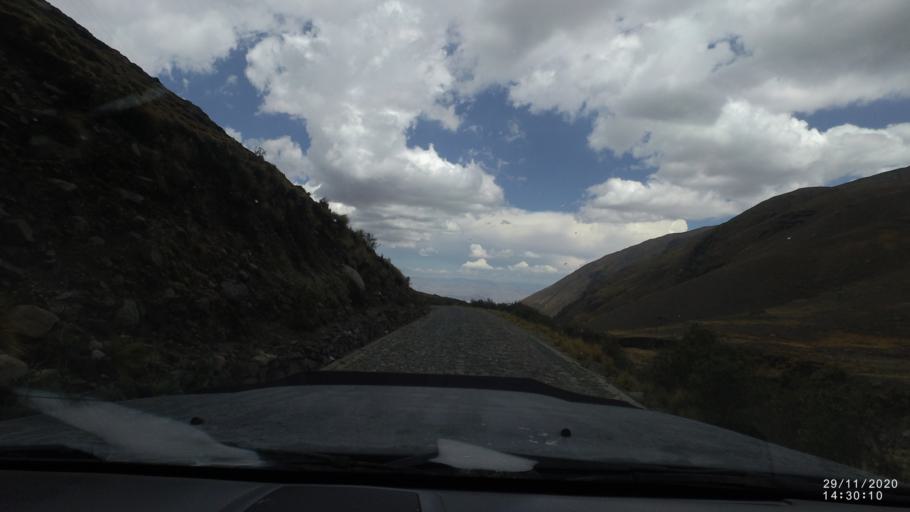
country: BO
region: Cochabamba
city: Sipe Sipe
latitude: -17.2630
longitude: -66.3507
